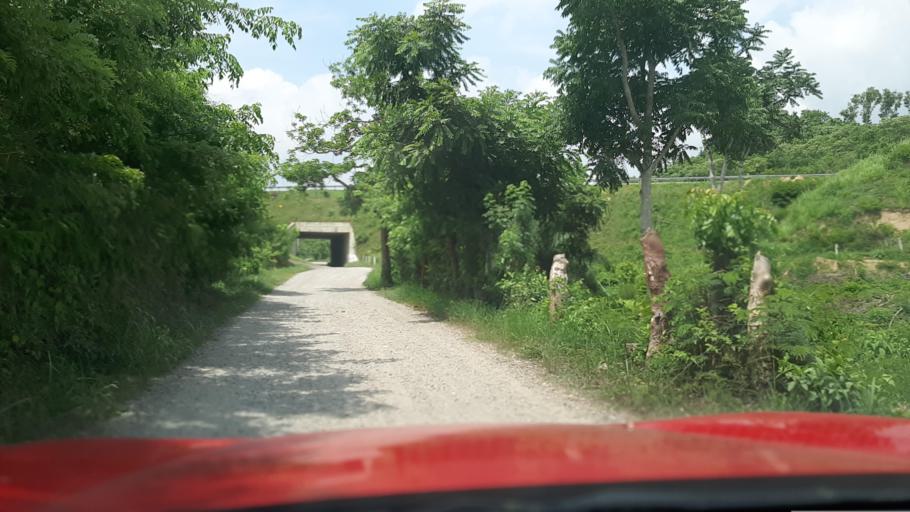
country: MX
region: Veracruz
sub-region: Papantla
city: Polutla
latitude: 20.4523
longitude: -97.2414
